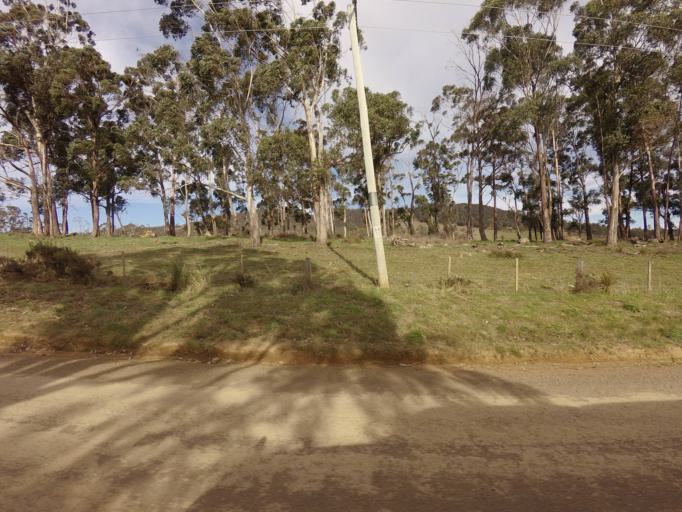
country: AU
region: Tasmania
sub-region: Huon Valley
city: Huonville
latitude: -43.0745
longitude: 147.0570
